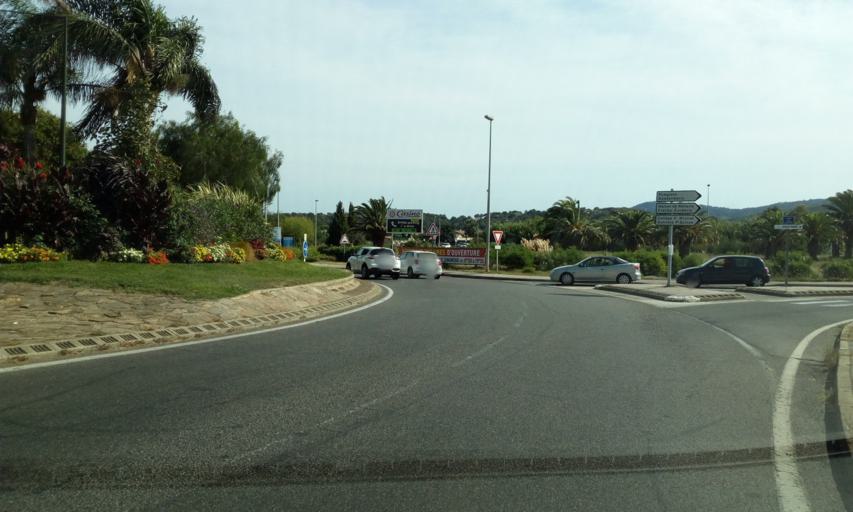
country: FR
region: Provence-Alpes-Cote d'Azur
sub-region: Departement du Var
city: Bormes-les-Mimosas
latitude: 43.1389
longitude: 6.3512
